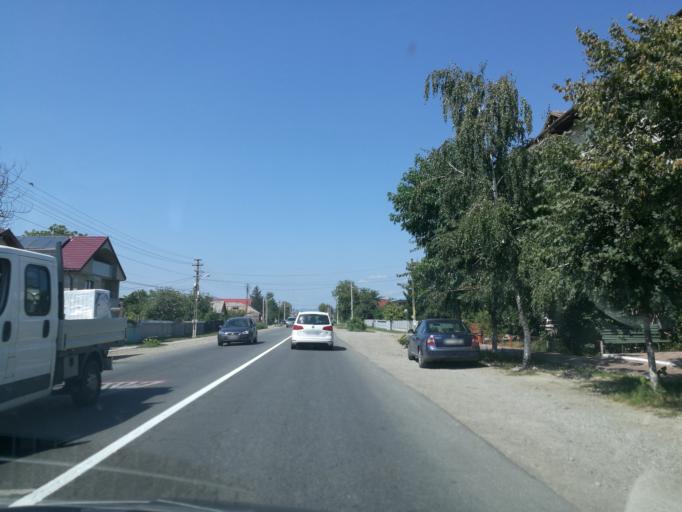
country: RO
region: Neamt
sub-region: Comuna Roznov
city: Roznov
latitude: 46.8390
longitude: 26.5056
